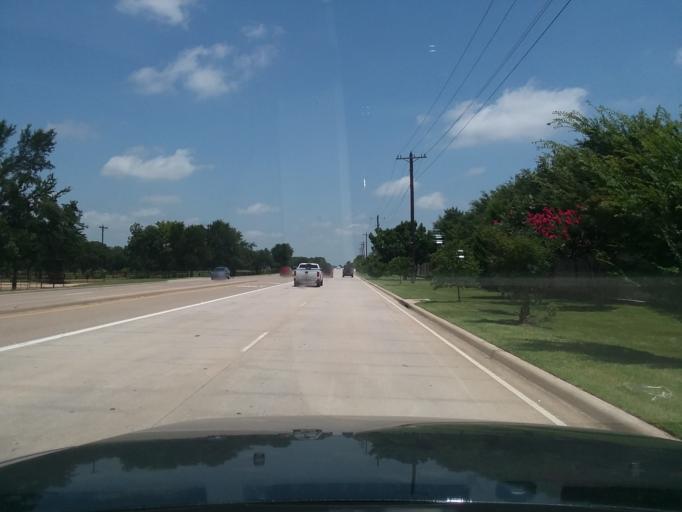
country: US
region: Texas
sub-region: Denton County
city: Bartonville
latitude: 33.0830
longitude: -97.1311
